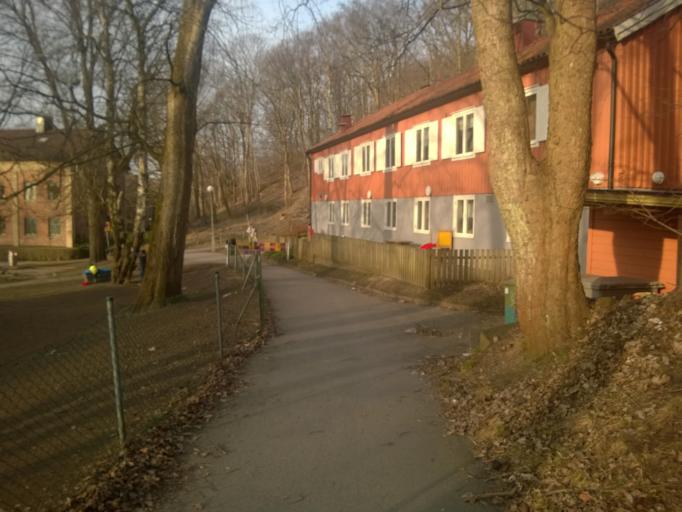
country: SE
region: Vaestra Goetaland
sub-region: Goteborg
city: Goeteborg
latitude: 57.6905
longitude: 11.9603
